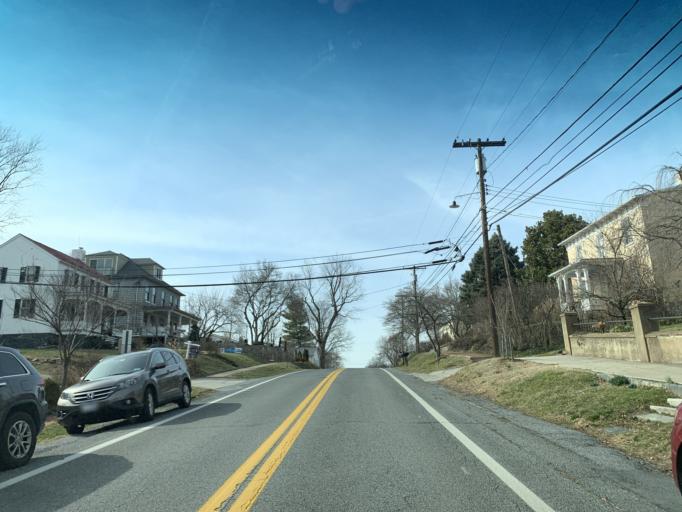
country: US
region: West Virginia
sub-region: Jefferson County
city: Bolivar
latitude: 39.3255
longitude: -77.7392
